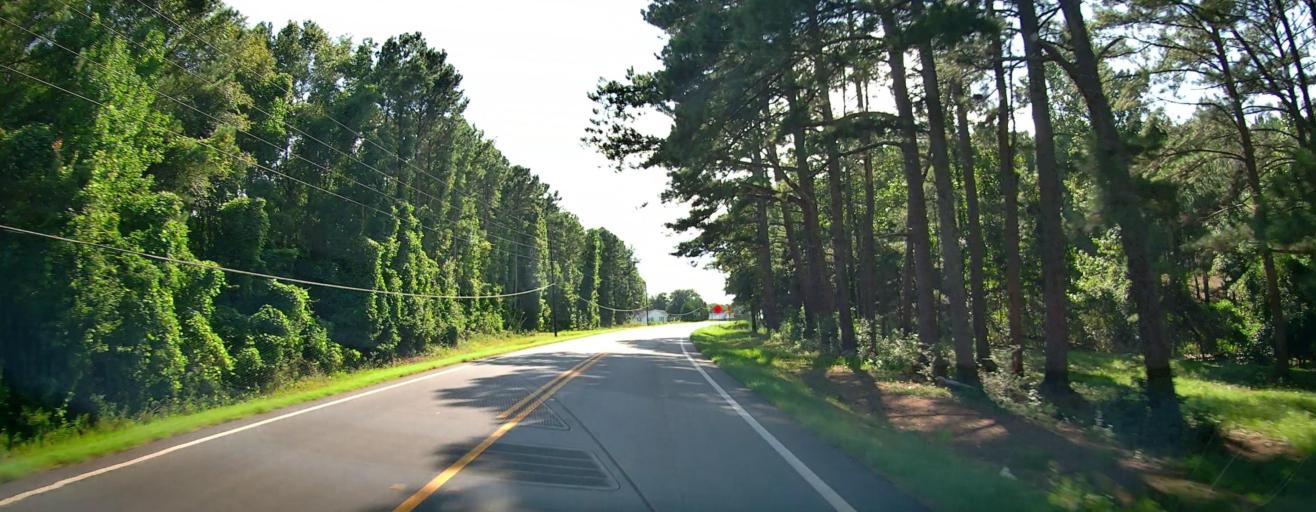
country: US
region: Georgia
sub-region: Upson County
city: Hannahs Mill
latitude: 32.9005
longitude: -84.3827
